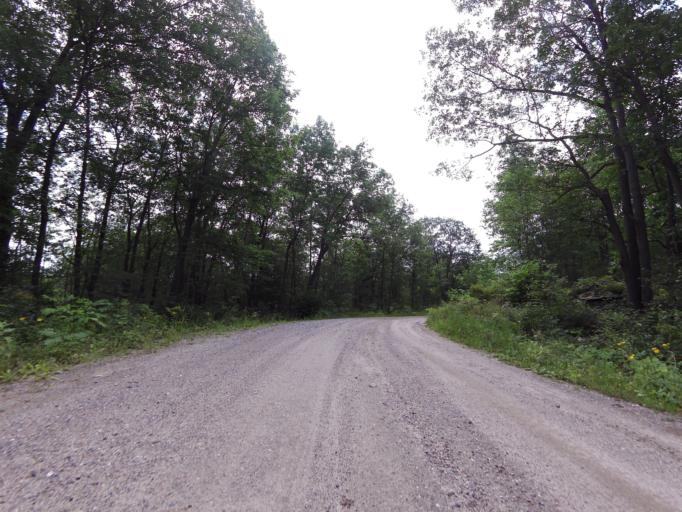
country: CA
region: Ontario
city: Perth
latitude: 44.7655
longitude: -76.6143
